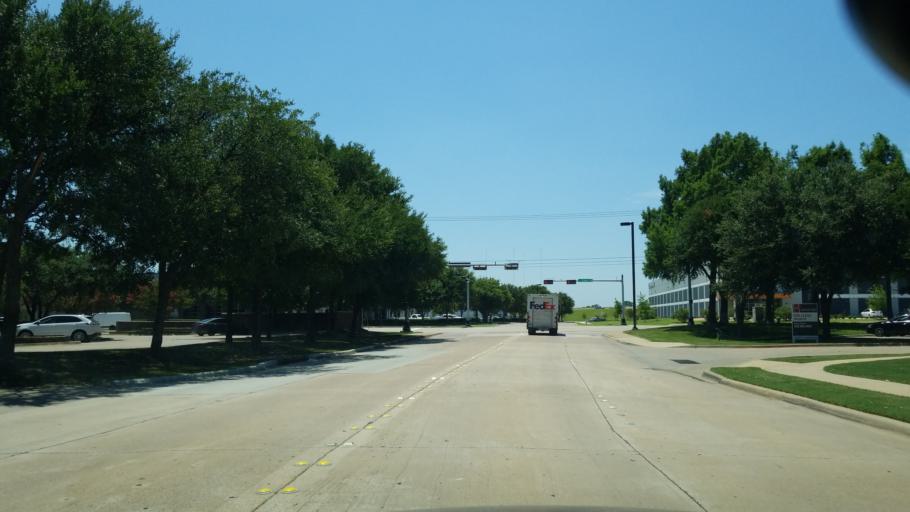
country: US
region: Texas
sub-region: Dallas County
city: Farmers Branch
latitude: 32.9452
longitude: -96.9242
